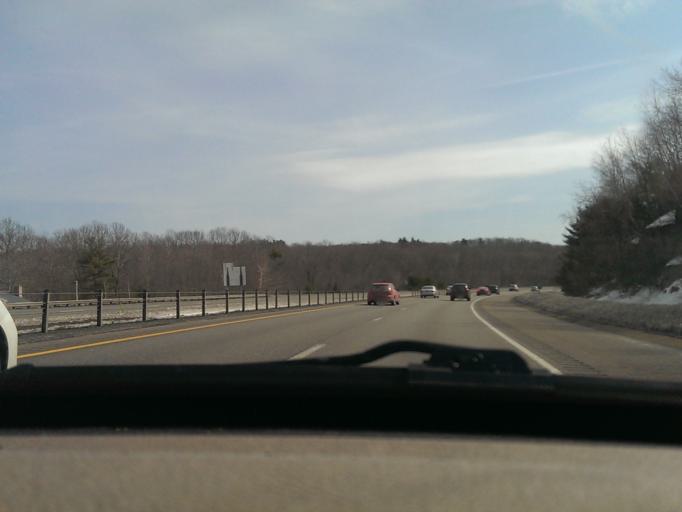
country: US
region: Massachusetts
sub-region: Worcester County
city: Whitinsville
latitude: 42.1356
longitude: -71.7038
